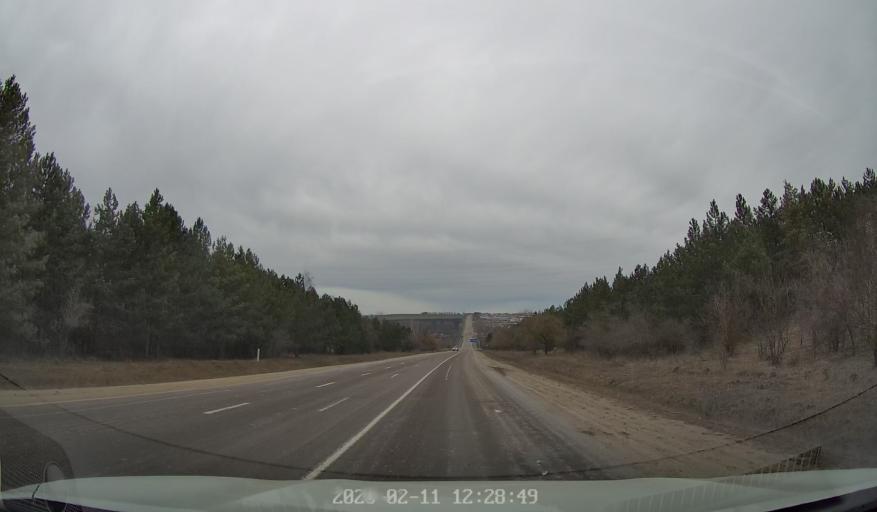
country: MD
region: Raionul Edinet
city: Edinet
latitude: 48.1483
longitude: 27.2952
